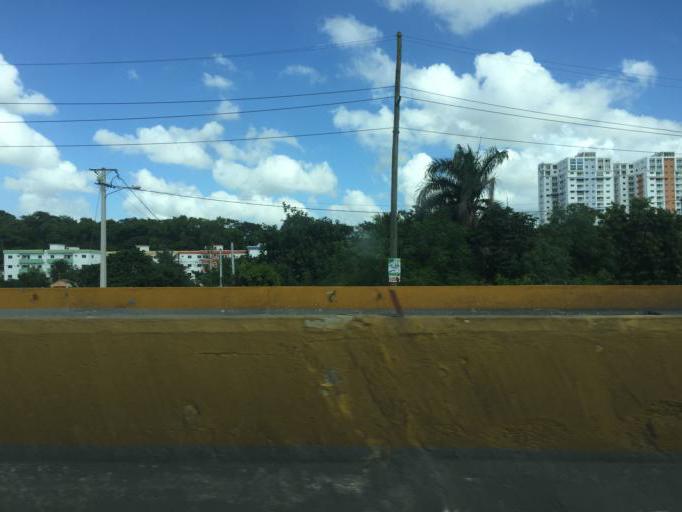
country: DO
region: Santo Domingo
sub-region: Santo Domingo
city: Santo Domingo Este
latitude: 18.4819
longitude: -69.8441
